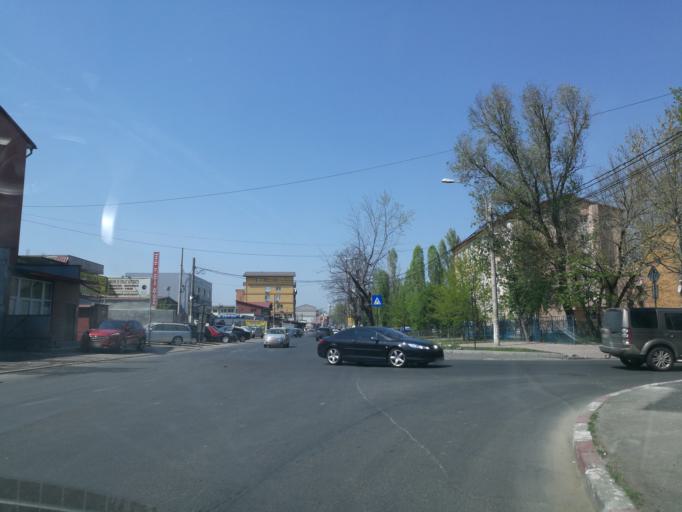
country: RO
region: Ilfov
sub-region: Comuna Popesti-Leordeni
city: Popesti-Leordeni
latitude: 44.4061
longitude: 26.1479
